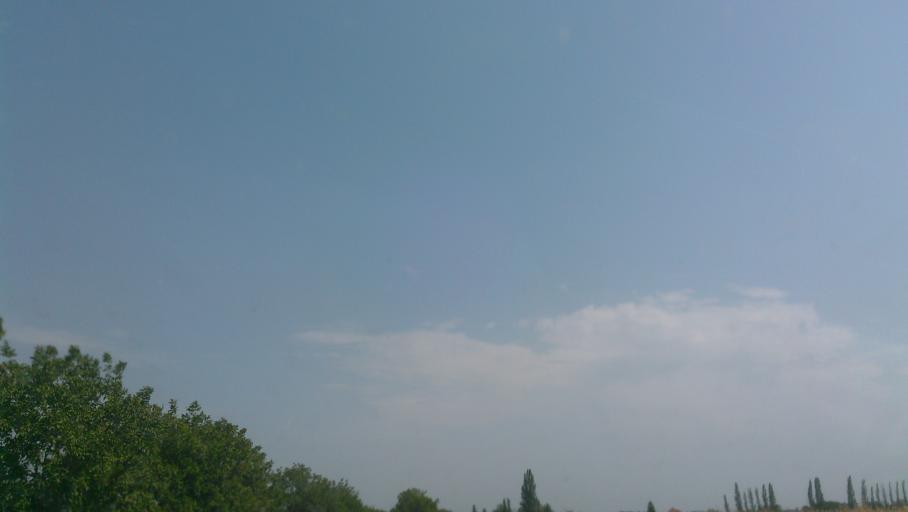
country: SK
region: Trnavsky
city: Dunajska Streda
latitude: 48.0393
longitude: 17.5233
